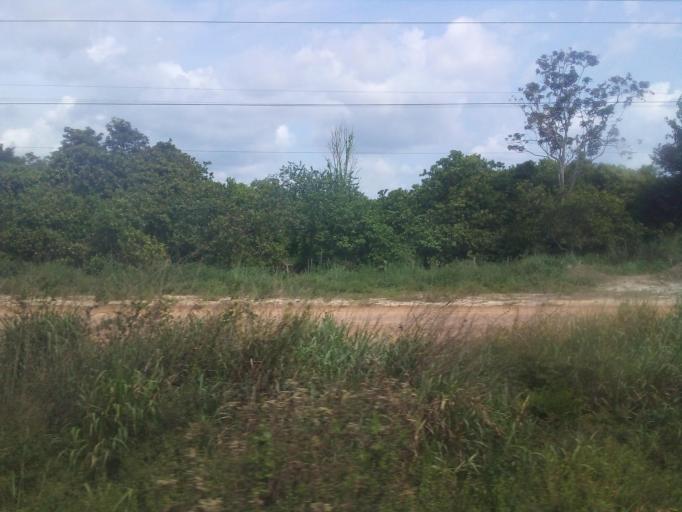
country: BR
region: Maranhao
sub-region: Santa Ines
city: Santa Ines
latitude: -3.8723
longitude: -46.1958
